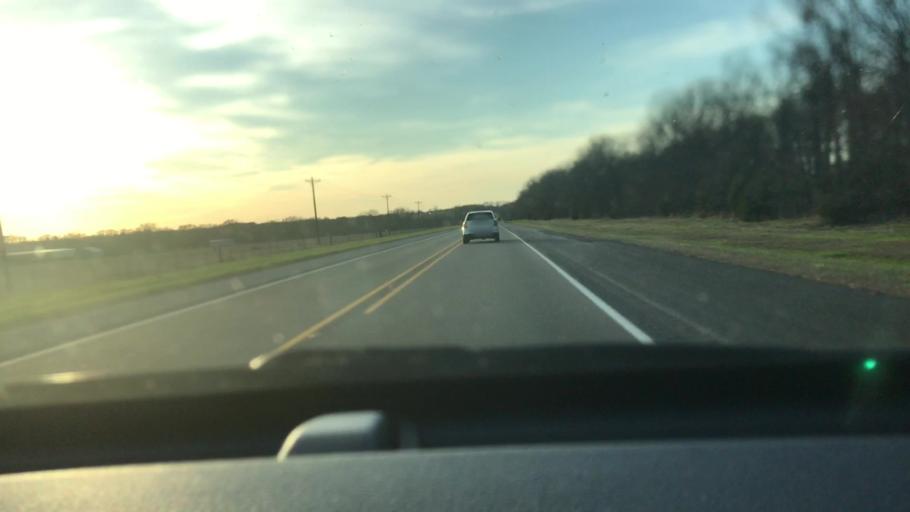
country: US
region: Texas
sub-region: Red River County
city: Clarksville
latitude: 33.5986
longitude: -94.9724
